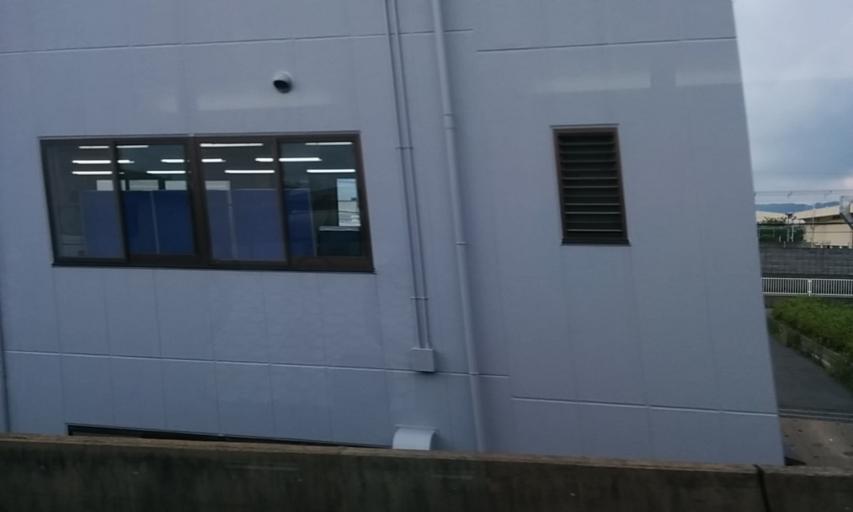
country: JP
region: Nara
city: Tenri
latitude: 34.6165
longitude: 135.7810
